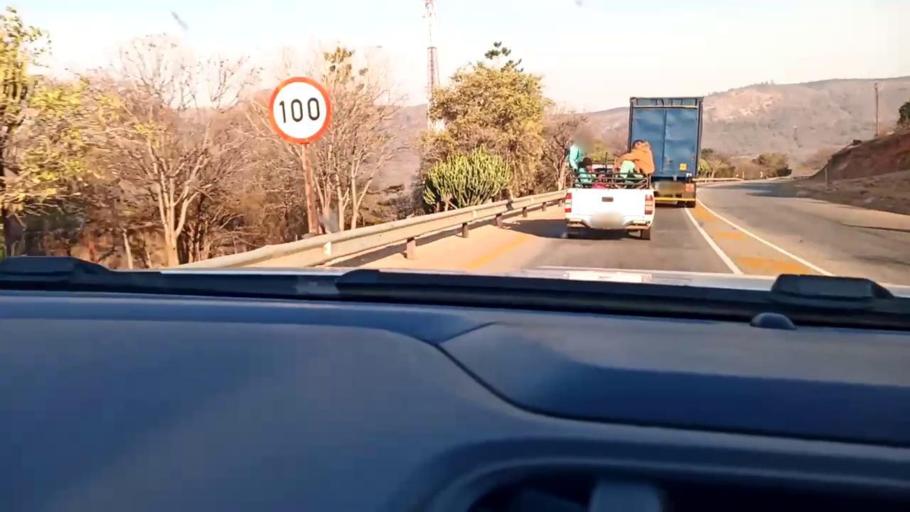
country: ZA
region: Limpopo
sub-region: Mopani District Municipality
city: Ga-Kgapane
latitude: -23.6475
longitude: 30.1707
